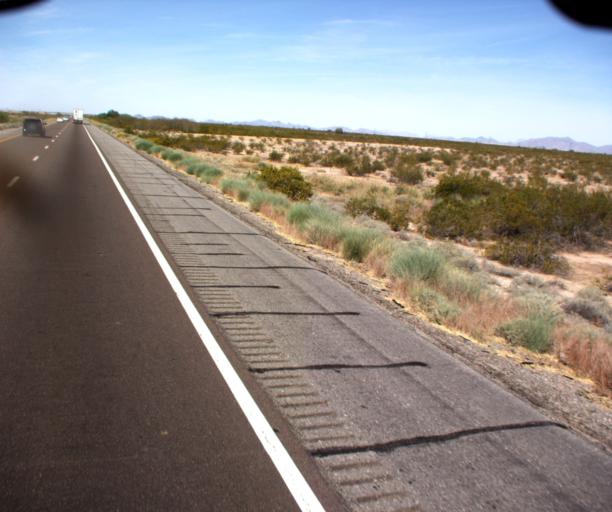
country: US
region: Arizona
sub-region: La Paz County
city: Salome
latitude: 33.5583
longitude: -113.2802
